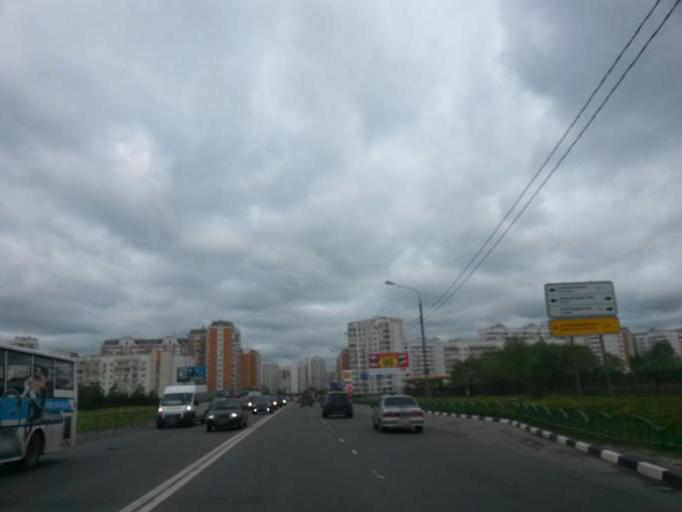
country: RU
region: Moscow
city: Kapotnya
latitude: 55.6597
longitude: 37.7831
